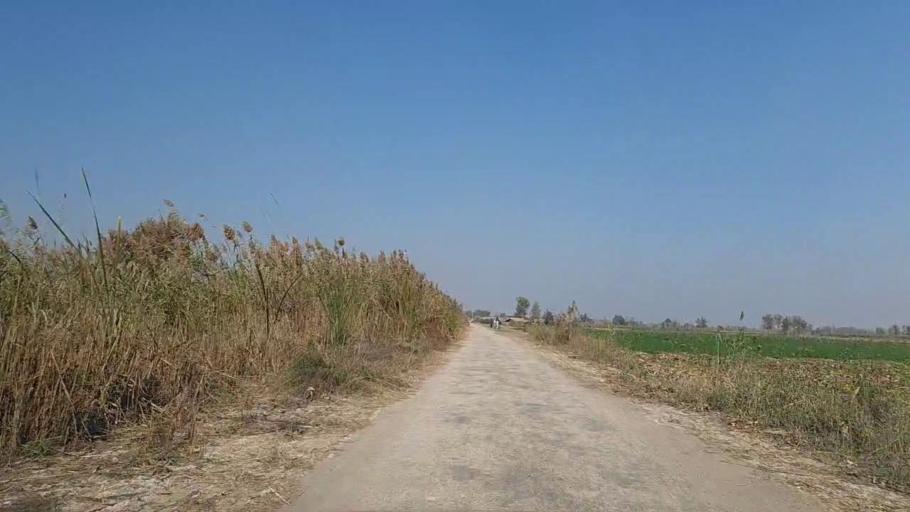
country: PK
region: Sindh
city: Daur
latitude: 26.5044
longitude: 68.3464
